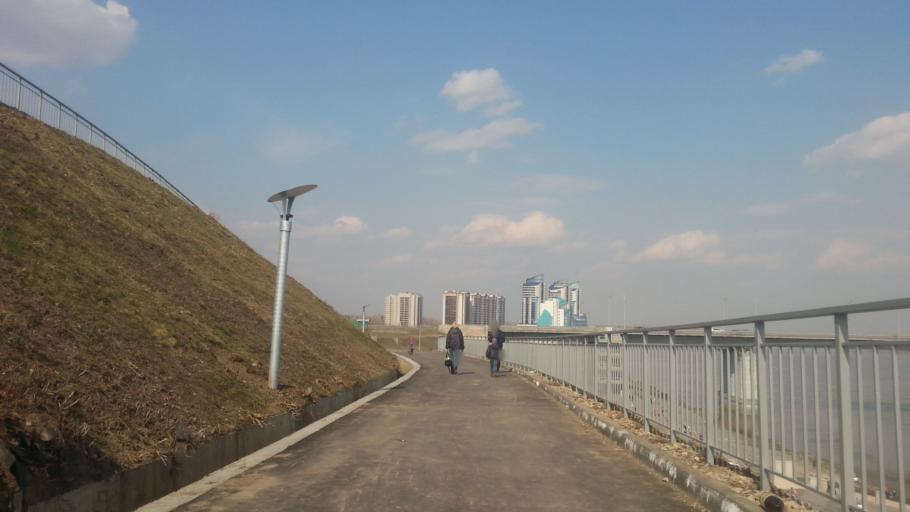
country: RU
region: Altai Krai
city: Zaton
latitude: 53.3228
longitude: 83.7973
